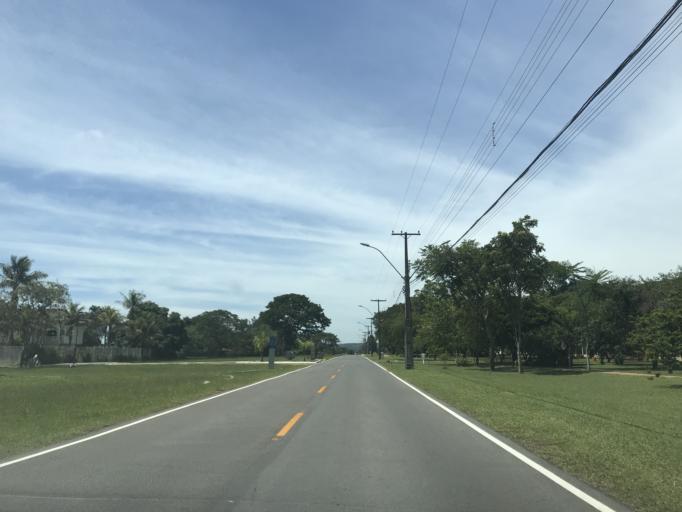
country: BR
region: Federal District
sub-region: Brasilia
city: Brasilia
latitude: -15.9047
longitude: -47.9337
